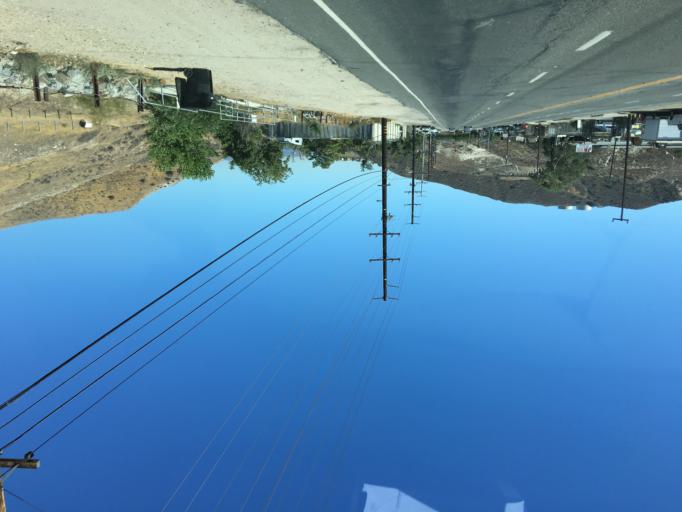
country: US
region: California
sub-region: Los Angeles County
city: Agua Dulce
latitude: 34.4408
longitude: -118.4303
